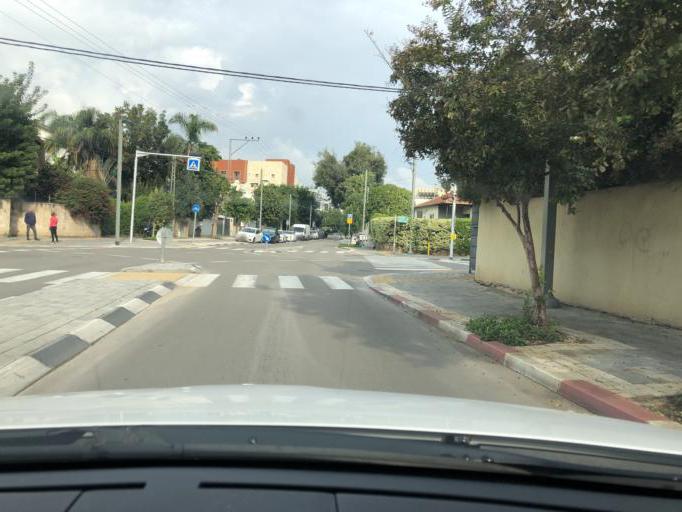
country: IL
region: Tel Aviv
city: Giv`atayim
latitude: 32.0541
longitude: 34.8231
